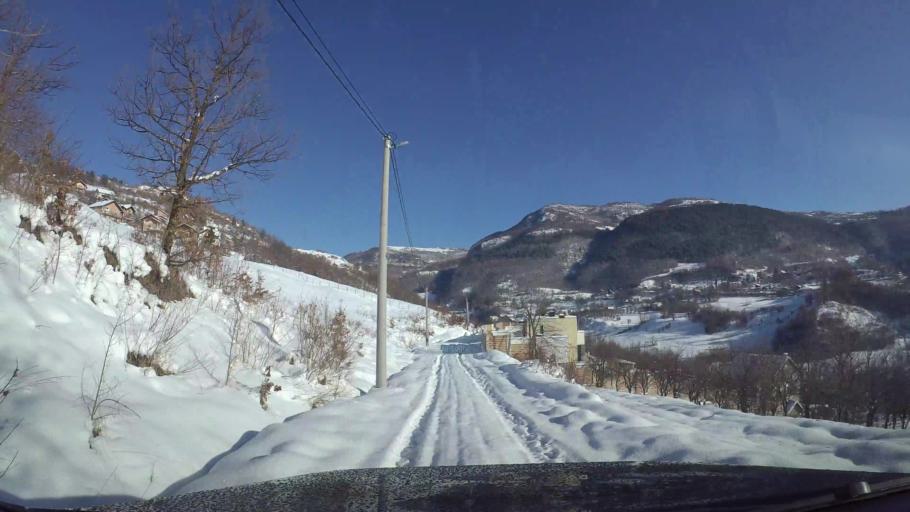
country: BA
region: Federation of Bosnia and Herzegovina
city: Kobilja Glava
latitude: 43.8939
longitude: 18.4087
